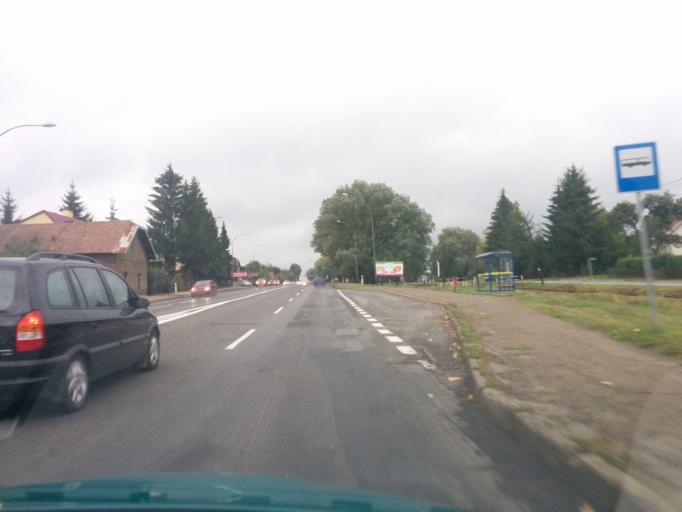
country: PL
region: Subcarpathian Voivodeship
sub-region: Powiat sanocki
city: Sanok
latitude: 49.5672
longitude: 22.1711
